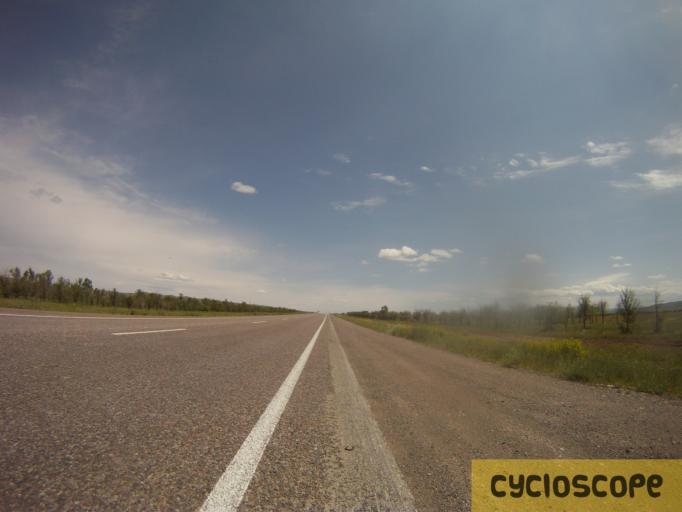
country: KZ
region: Zhambyl
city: Georgiyevka
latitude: 43.3112
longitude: 74.9135
